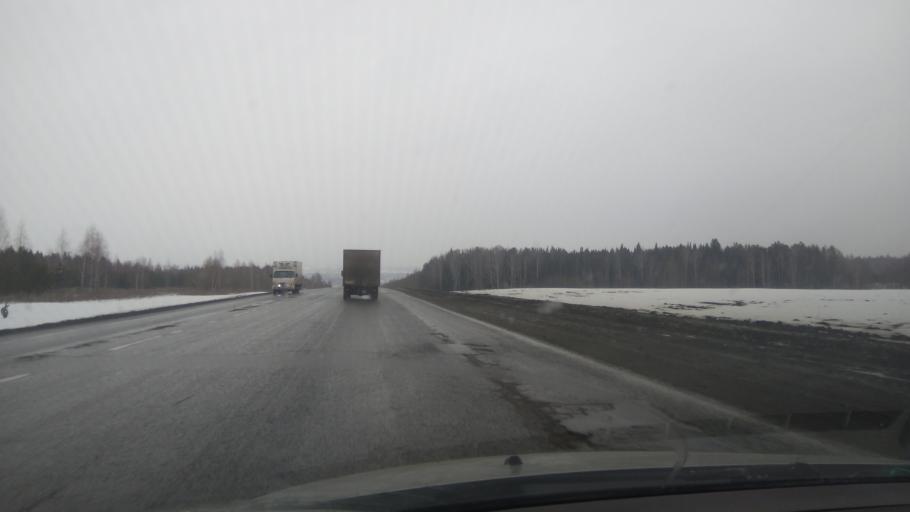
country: RU
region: Perm
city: Kungur
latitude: 57.3453
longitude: 56.9403
